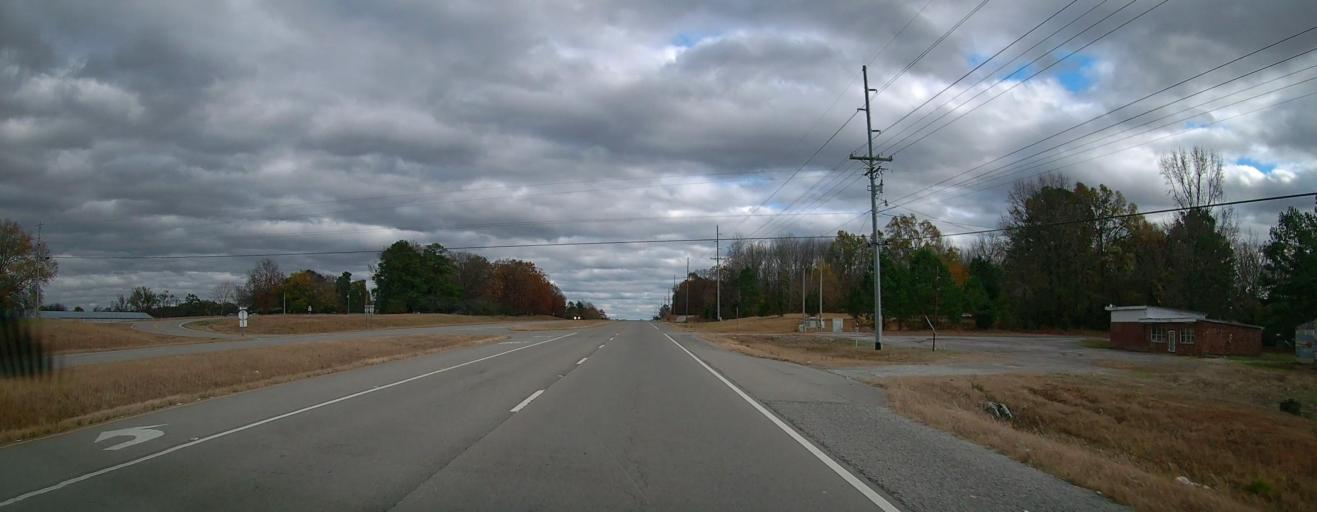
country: US
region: Alabama
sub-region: Lawrence County
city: Town Creek
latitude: 34.5705
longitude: -87.3849
